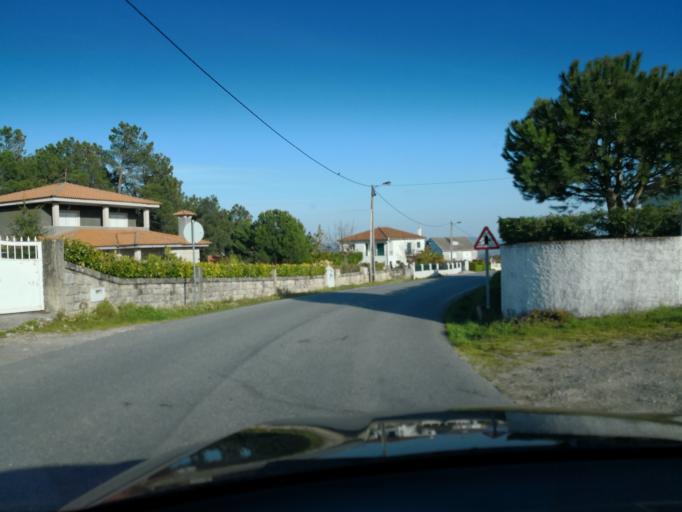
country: PT
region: Vila Real
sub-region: Sabrosa
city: Sabrosa
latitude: 41.3568
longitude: -7.6143
